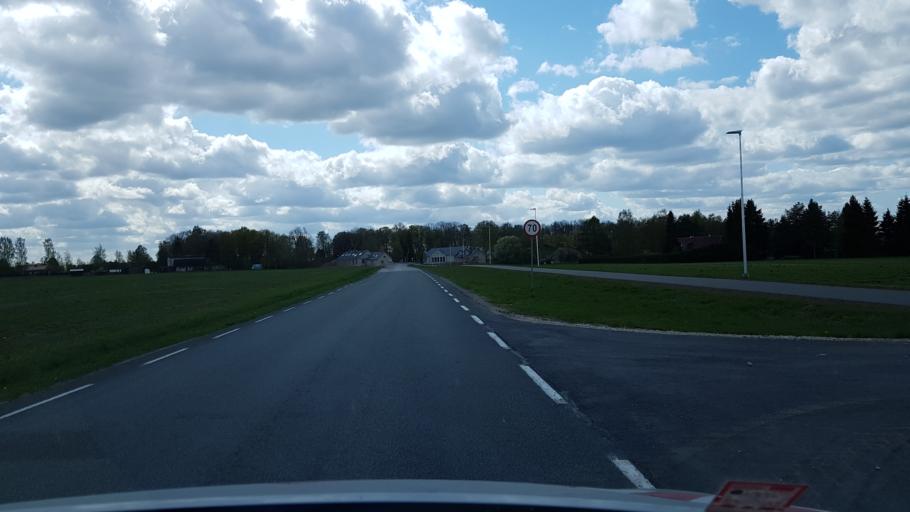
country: EE
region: Jogevamaa
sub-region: Poltsamaa linn
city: Poltsamaa
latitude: 58.7105
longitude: 25.9414
